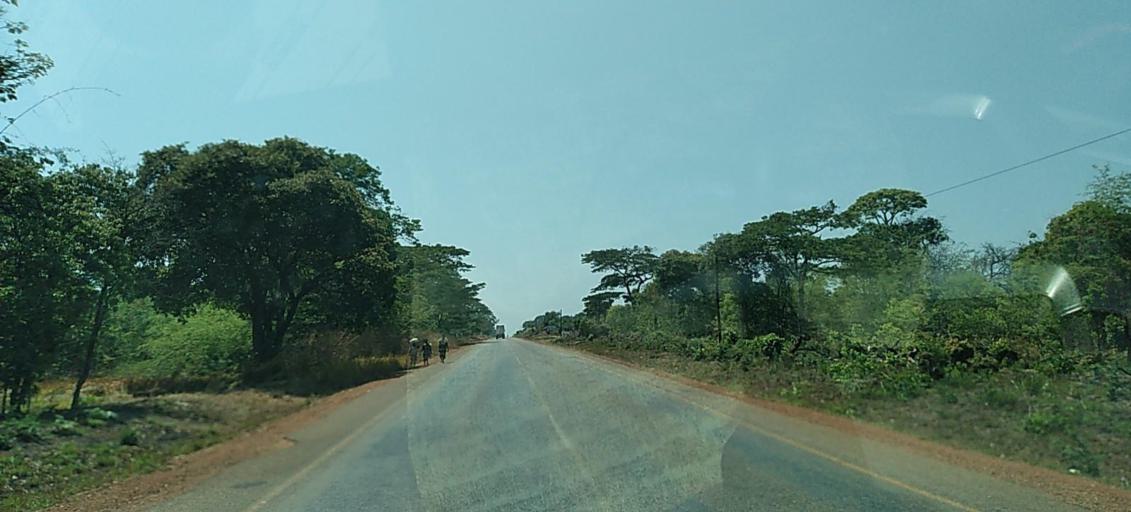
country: ZM
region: North-Western
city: Solwezi
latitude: -12.3450
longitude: 25.9117
